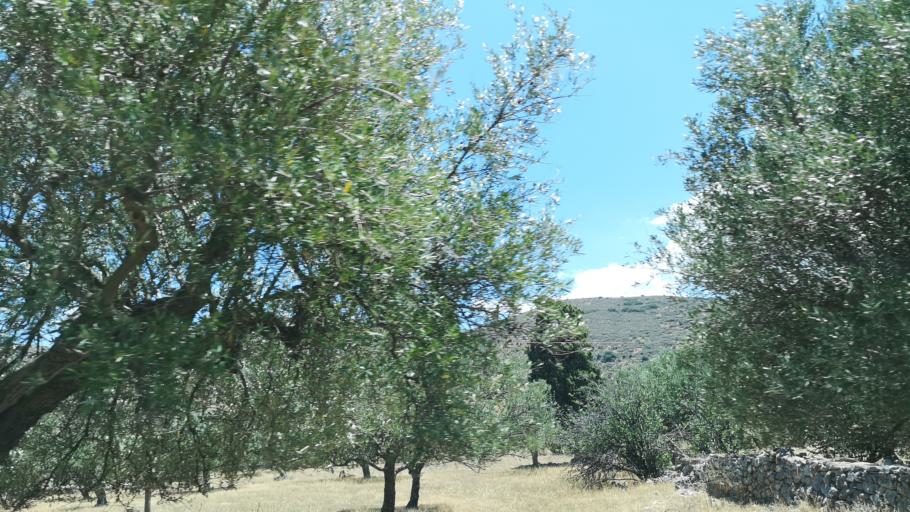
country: GR
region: Crete
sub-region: Nomos Lasithiou
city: Neapoli
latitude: 35.2593
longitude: 25.6474
